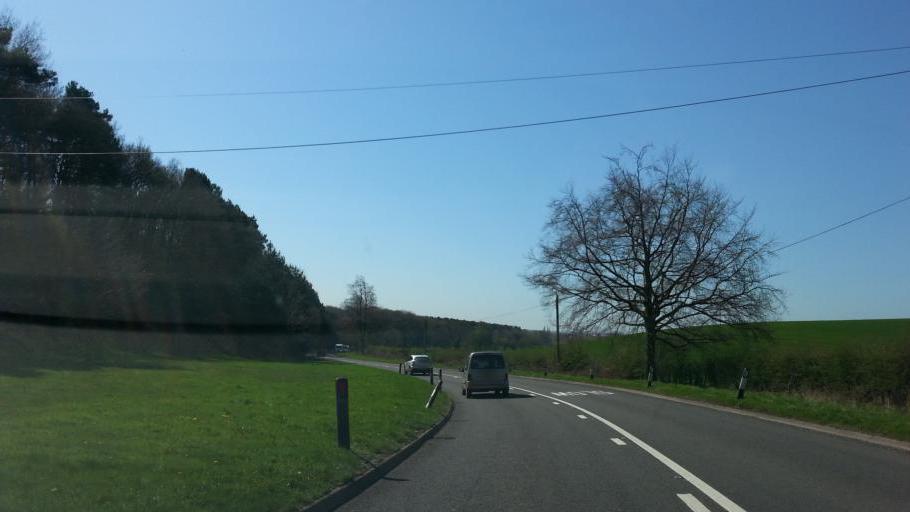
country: GB
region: England
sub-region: Staffordshire
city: Stafford
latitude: 52.8237
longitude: -2.0705
